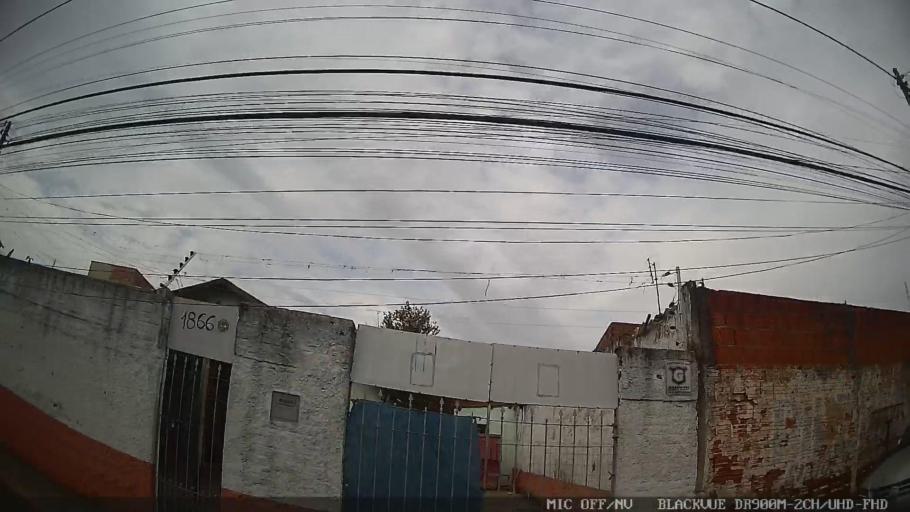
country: BR
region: Sao Paulo
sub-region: Salto
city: Salto
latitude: -23.2188
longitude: -47.2649
